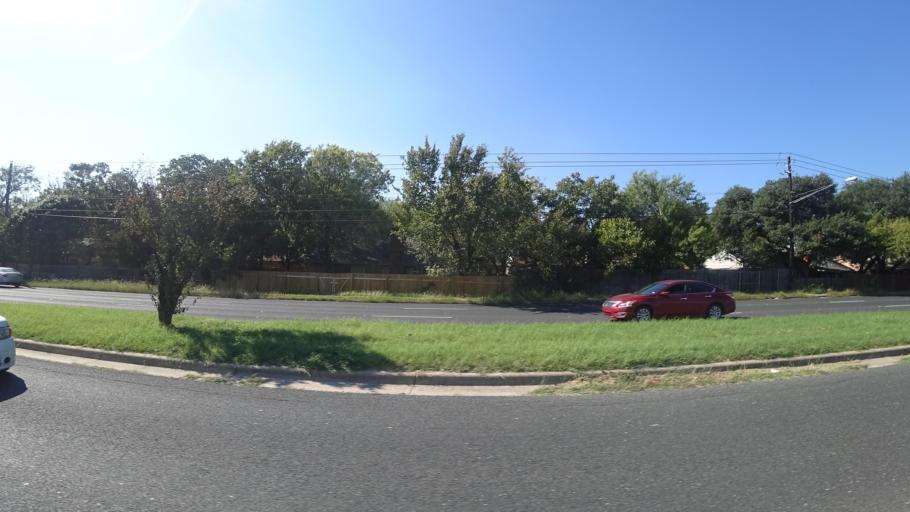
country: US
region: Texas
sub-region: Travis County
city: Wells Branch
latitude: 30.3604
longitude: -97.6697
